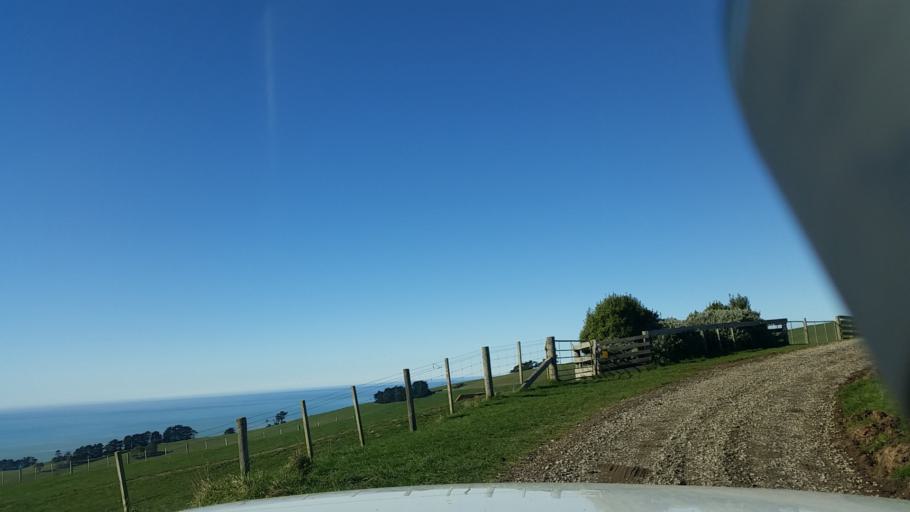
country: NZ
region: Canterbury
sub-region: Christchurch City
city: Christchurch
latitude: -43.6509
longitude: 172.9724
